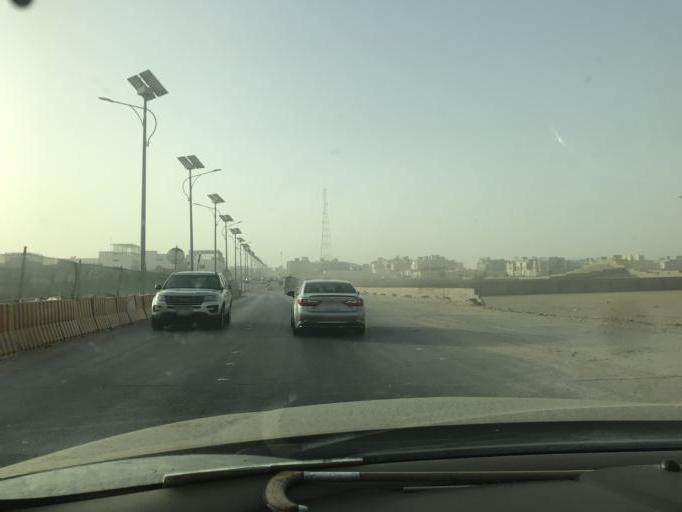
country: SA
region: Ar Riyad
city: Riyadh
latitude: 24.8453
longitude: 46.6644
